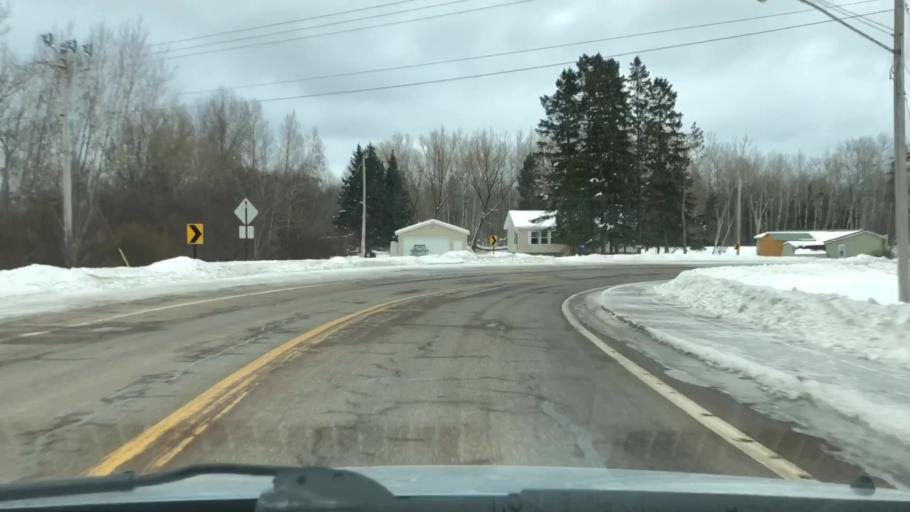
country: US
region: Minnesota
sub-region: Carlton County
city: Carlton
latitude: 46.6642
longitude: -92.3860
